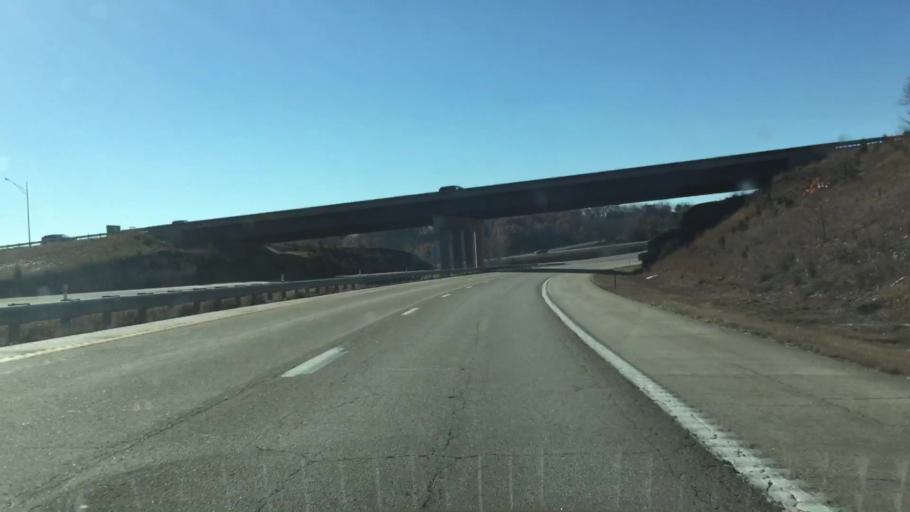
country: US
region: Missouri
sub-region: Cole County
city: Jefferson City
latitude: 38.5412
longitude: -92.2089
